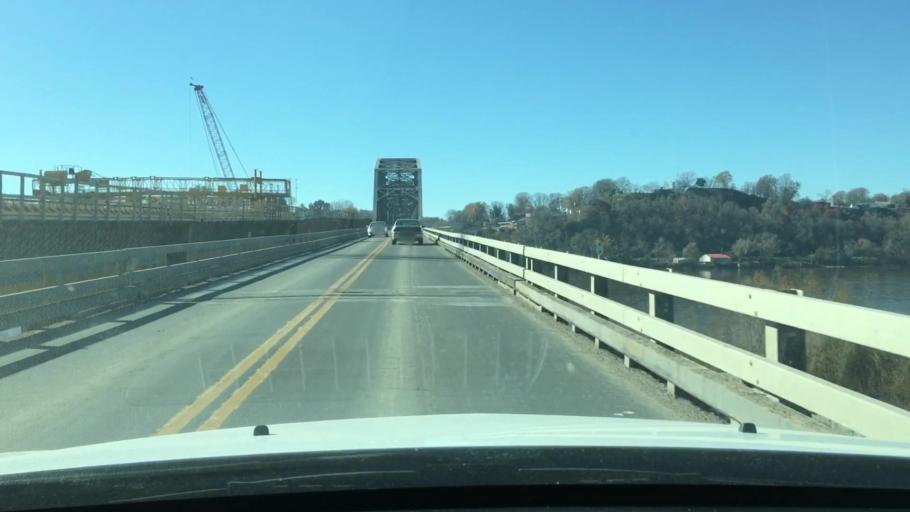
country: US
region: Missouri
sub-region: Pike County
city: Louisiana
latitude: 39.4586
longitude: -91.0441
